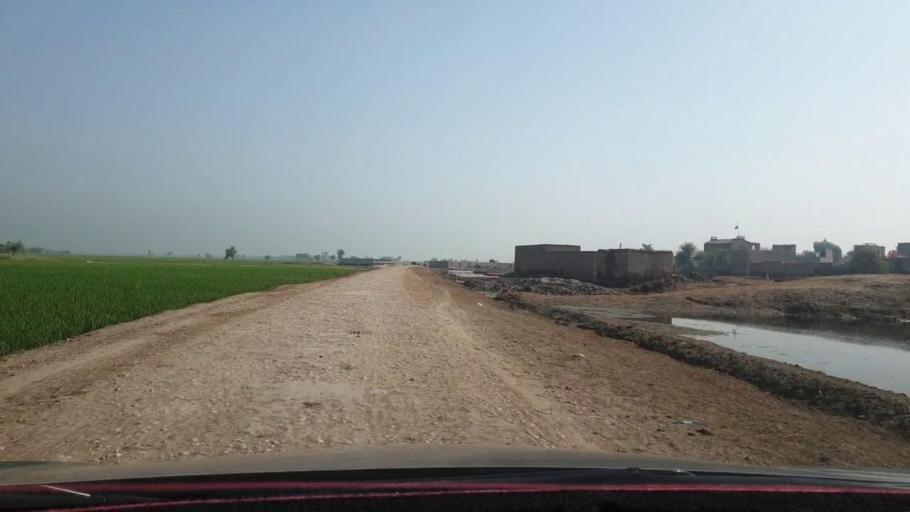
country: PK
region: Sindh
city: Nasirabad
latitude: 27.4627
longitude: 67.9189
